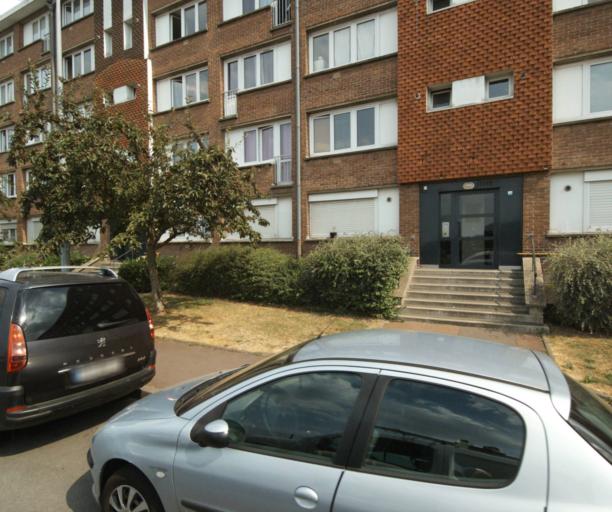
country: FR
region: Nord-Pas-de-Calais
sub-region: Departement du Nord
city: Tourcoing
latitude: 50.7245
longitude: 3.1370
